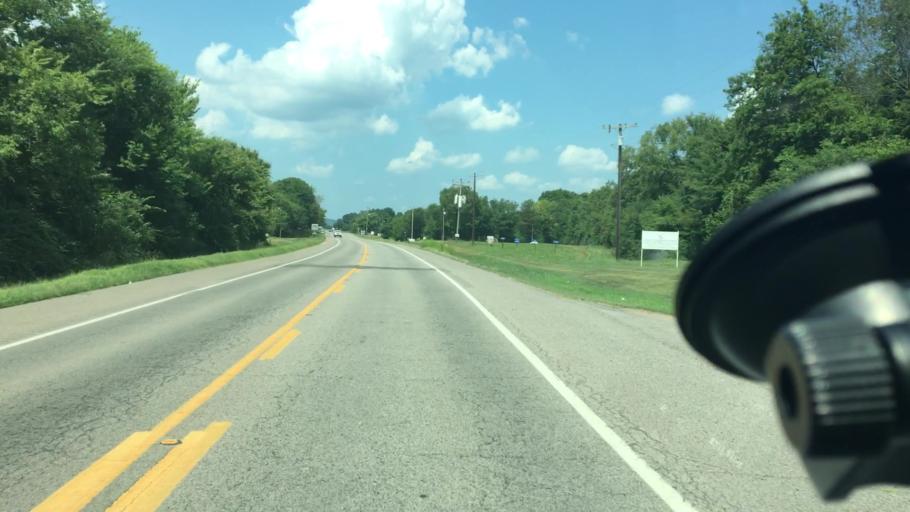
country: US
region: Arkansas
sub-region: Logan County
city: Paris
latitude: 35.2951
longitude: -93.6887
